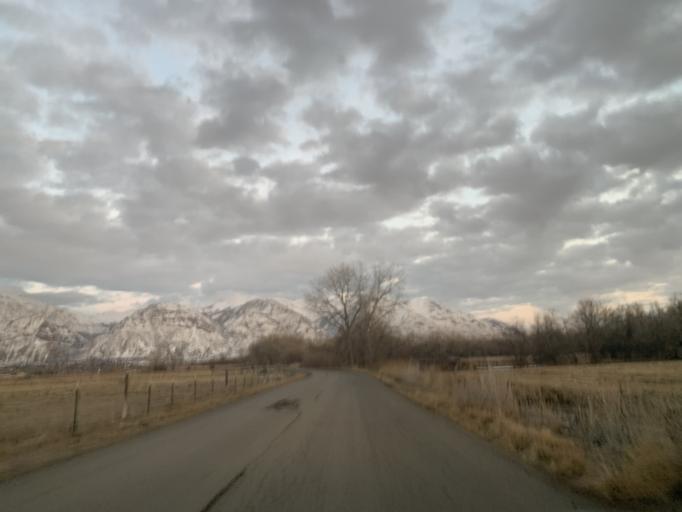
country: US
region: Utah
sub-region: Utah County
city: Orem
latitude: 40.2385
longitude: -111.7271
